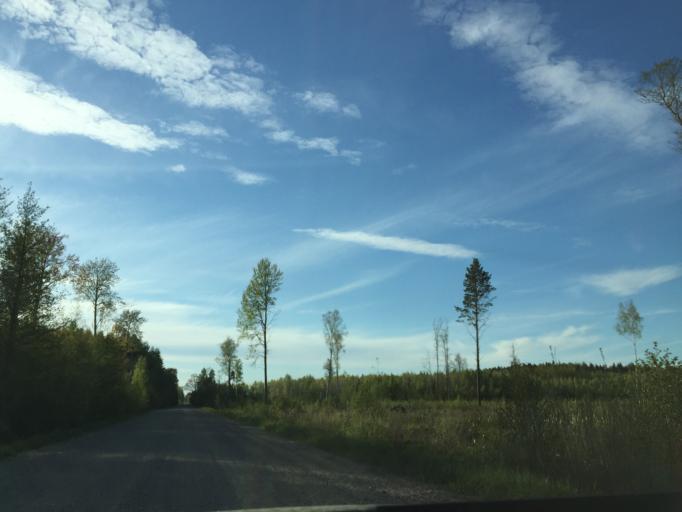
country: LV
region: Saulkrastu
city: Saulkrasti
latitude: 57.4064
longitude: 24.5424
